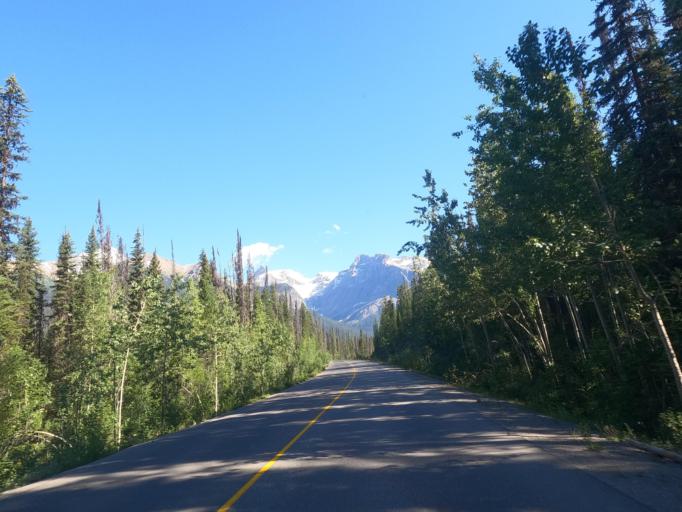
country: CA
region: Alberta
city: Lake Louise
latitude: 51.4166
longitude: -116.5335
